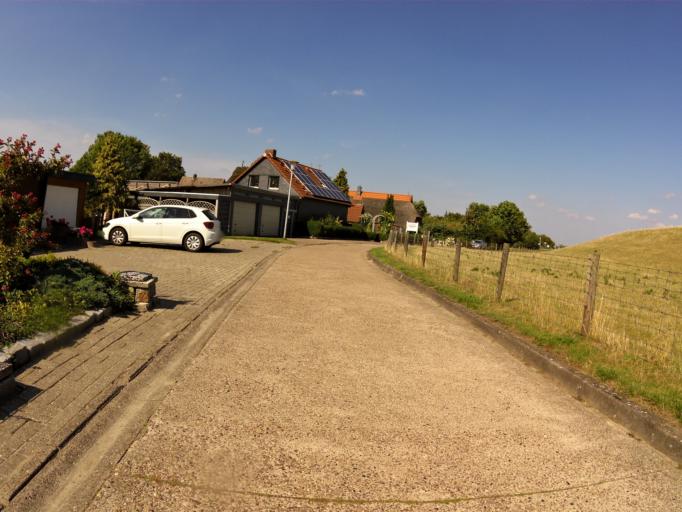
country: DE
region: Lower Saxony
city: Ovelgonne
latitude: 53.3933
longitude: 8.4591
